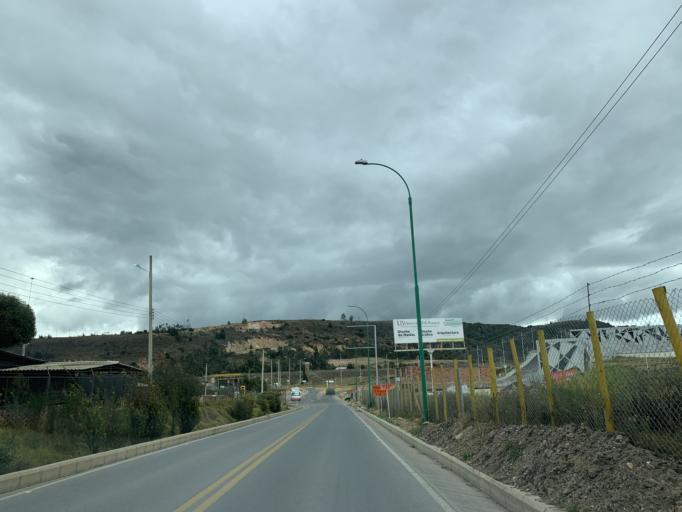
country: CO
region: Boyaca
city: Tunja
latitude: 5.5337
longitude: -73.3447
